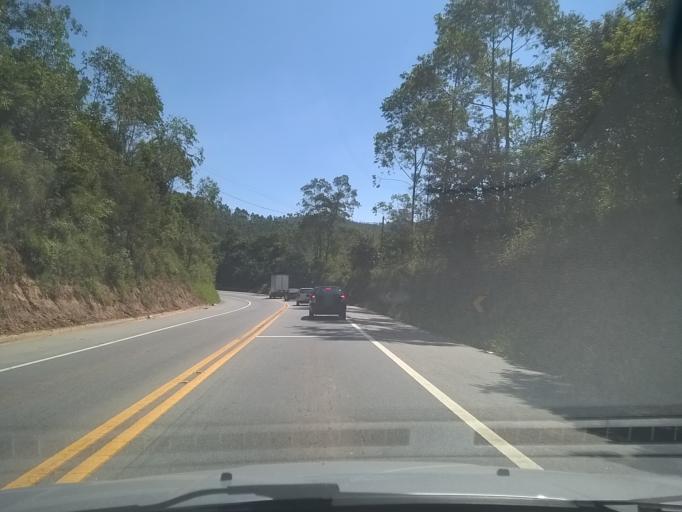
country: BR
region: Sao Paulo
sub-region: Francisco Morato
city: Francisco Morato
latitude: -23.2872
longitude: -46.7890
